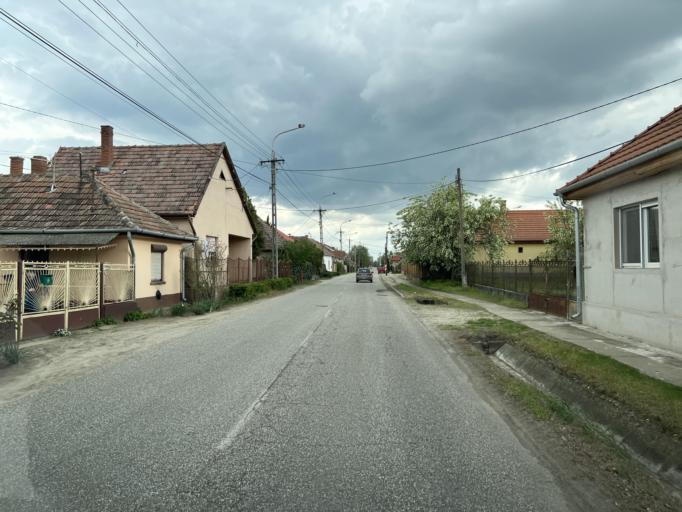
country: HU
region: Pest
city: Hernad
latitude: 47.1640
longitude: 19.4298
